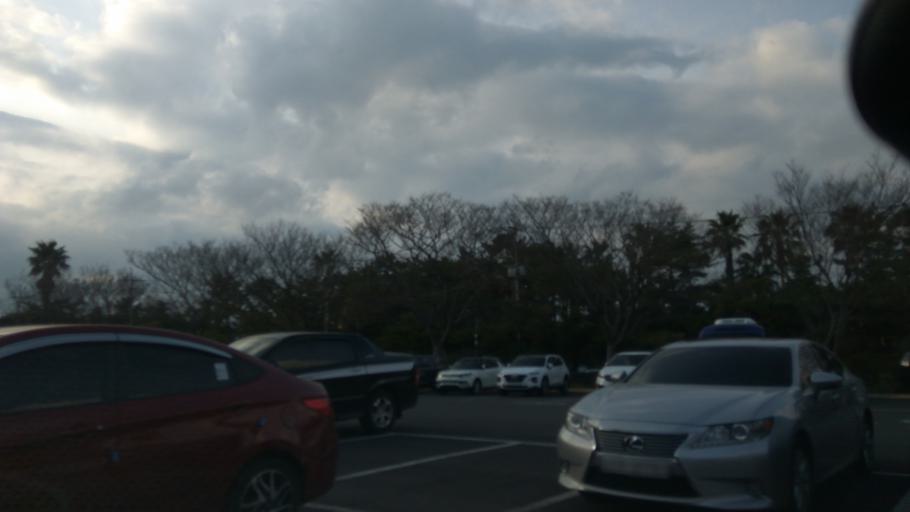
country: KR
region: Jeju-do
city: Gaigeturi
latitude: 33.3904
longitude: 126.2381
